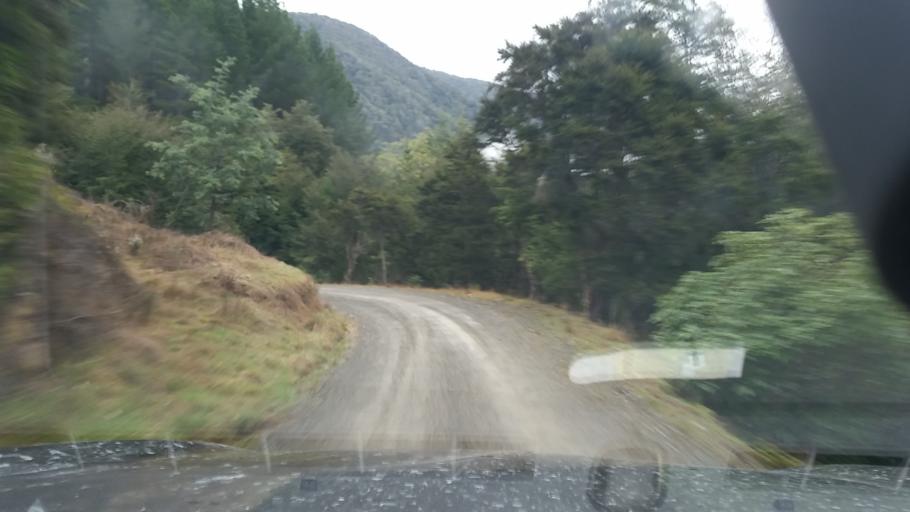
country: NZ
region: Nelson
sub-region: Nelson City
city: Nelson
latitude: -41.3723
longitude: 173.6022
